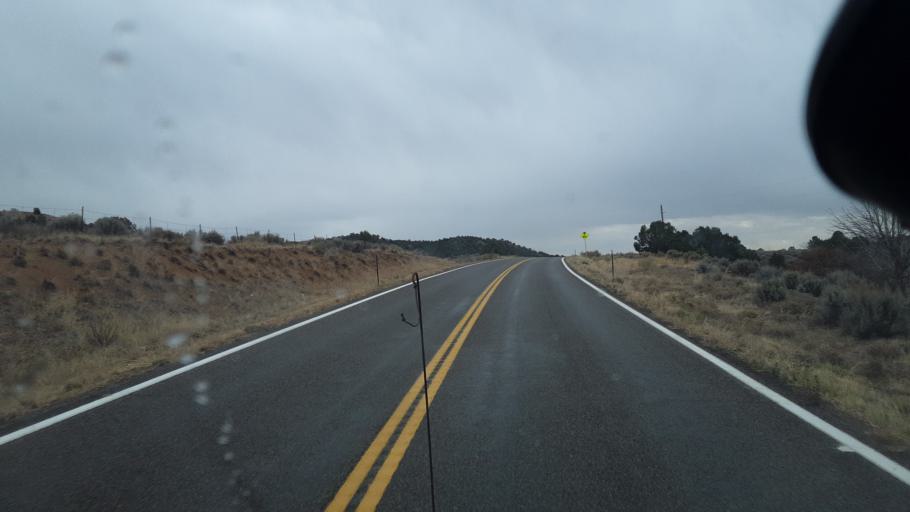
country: US
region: New Mexico
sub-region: San Juan County
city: Spencerville
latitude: 37.0412
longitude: -108.1824
